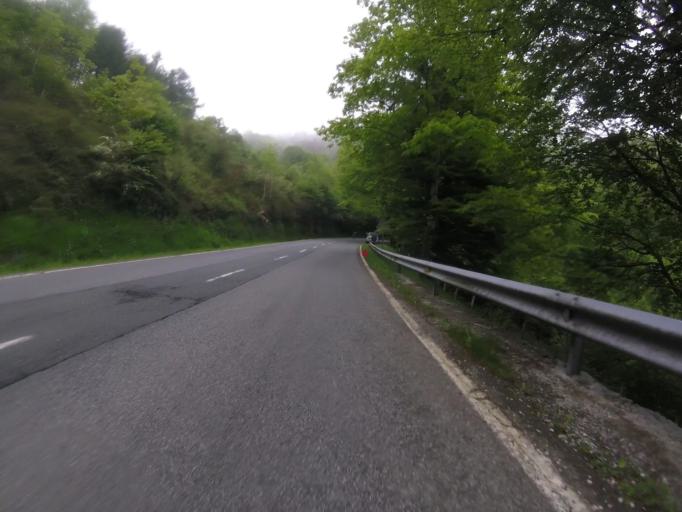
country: ES
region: Navarre
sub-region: Provincia de Navarra
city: Zugarramurdi
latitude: 43.2443
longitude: -1.4808
